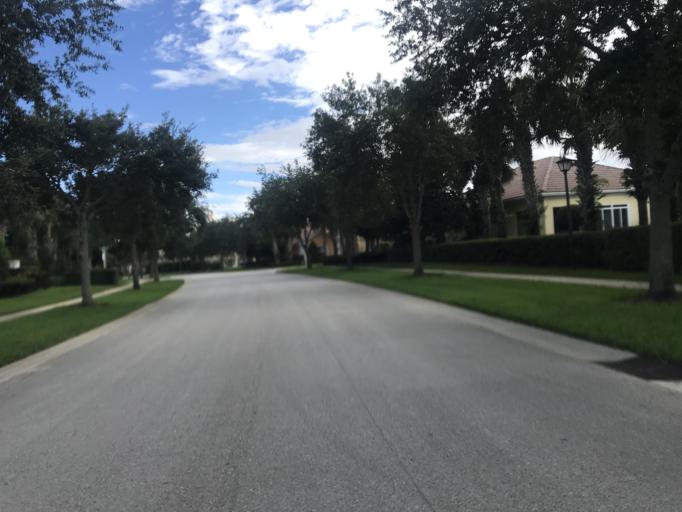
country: US
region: Florida
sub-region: Indian River County
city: Gifford
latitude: 27.6876
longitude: -80.4424
